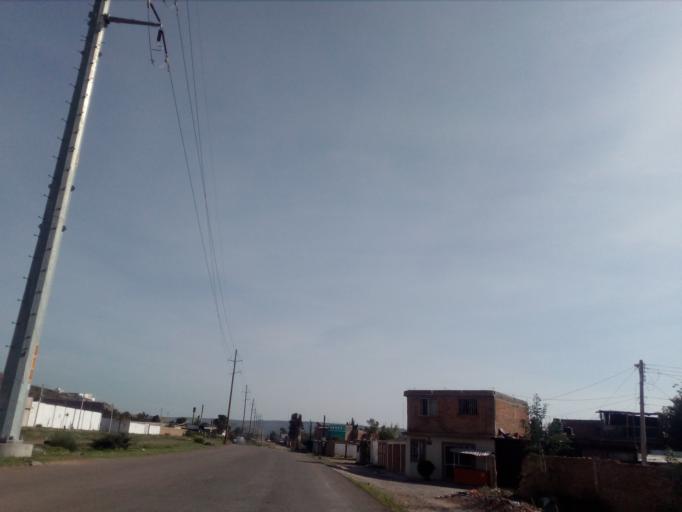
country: MX
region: Durango
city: Victoria de Durango
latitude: 24.0528
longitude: -104.6552
